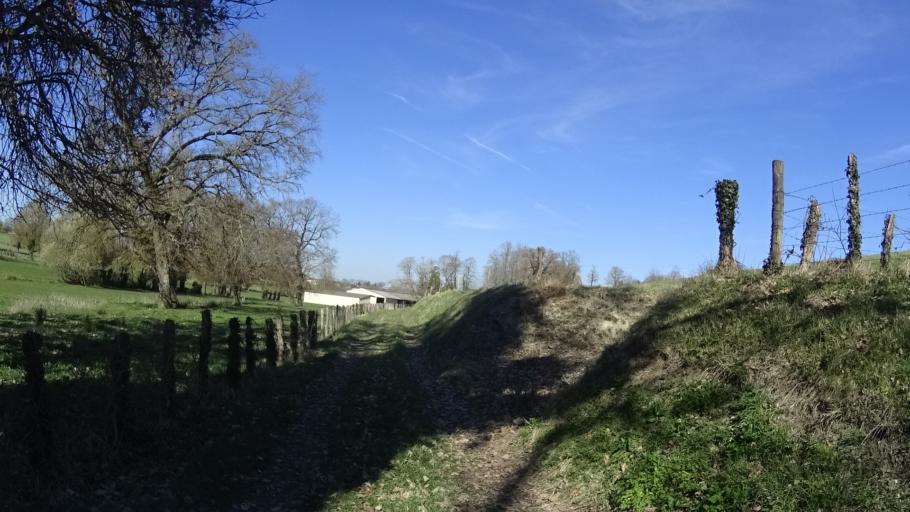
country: FR
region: Aquitaine
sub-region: Departement de la Dordogne
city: Riberac
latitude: 45.2284
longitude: 0.3341
